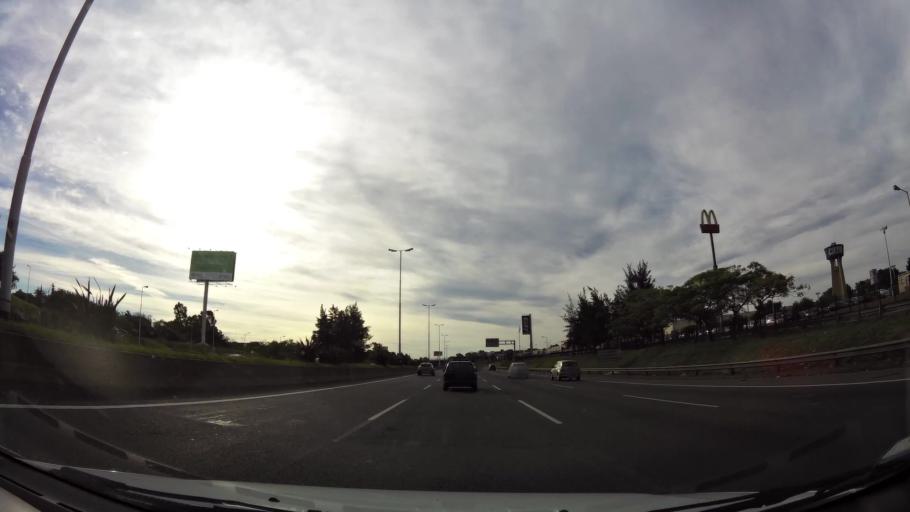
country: AR
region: Buenos Aires
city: Caseros
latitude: -34.6316
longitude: -58.5458
